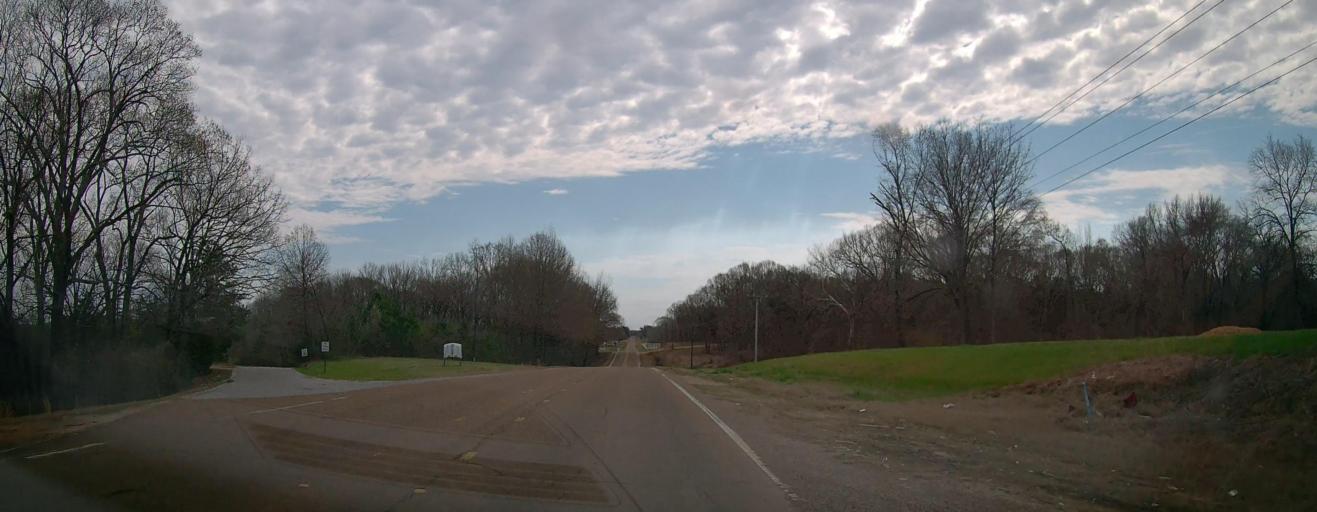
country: US
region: Mississippi
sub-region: Marshall County
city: Byhalia
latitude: 34.8603
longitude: -89.6534
